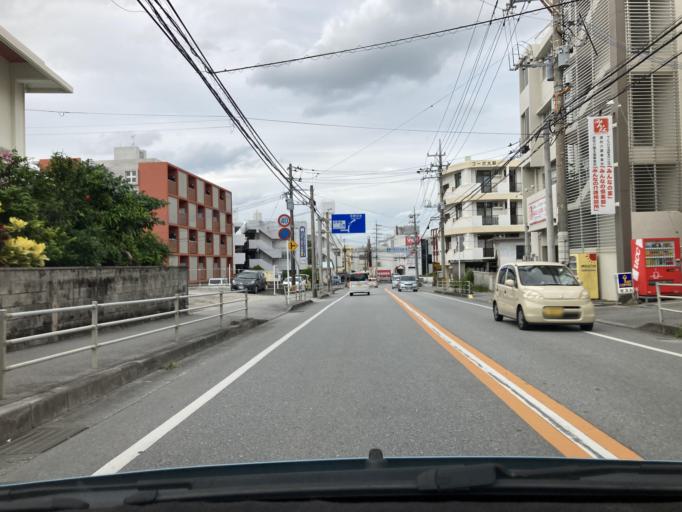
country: JP
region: Okinawa
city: Tomigusuku
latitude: 26.1864
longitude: 127.6806
